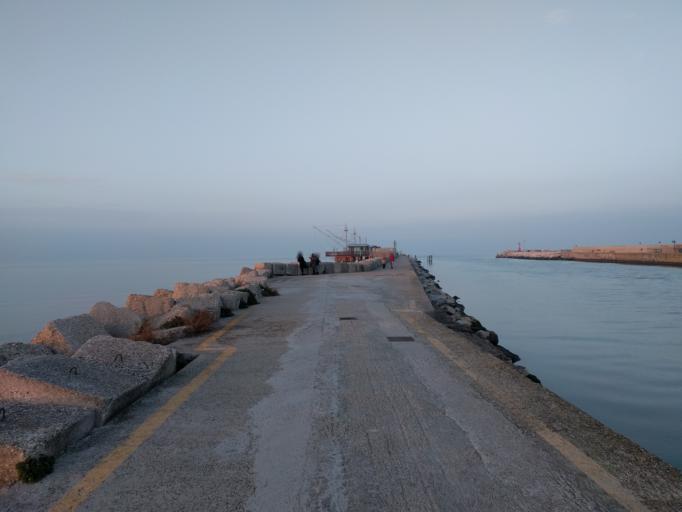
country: IT
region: The Marches
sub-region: Provincia di Pesaro e Urbino
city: Fano
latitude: 43.8532
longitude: 13.0150
